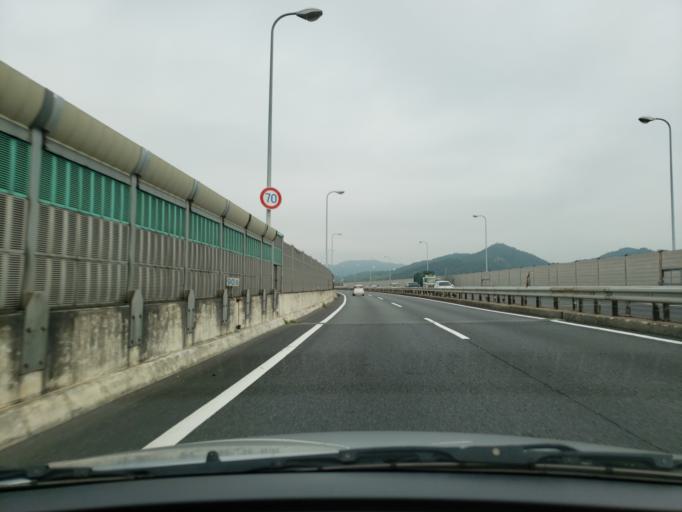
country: JP
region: Hyogo
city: Himeji
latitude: 34.8167
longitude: 134.6670
